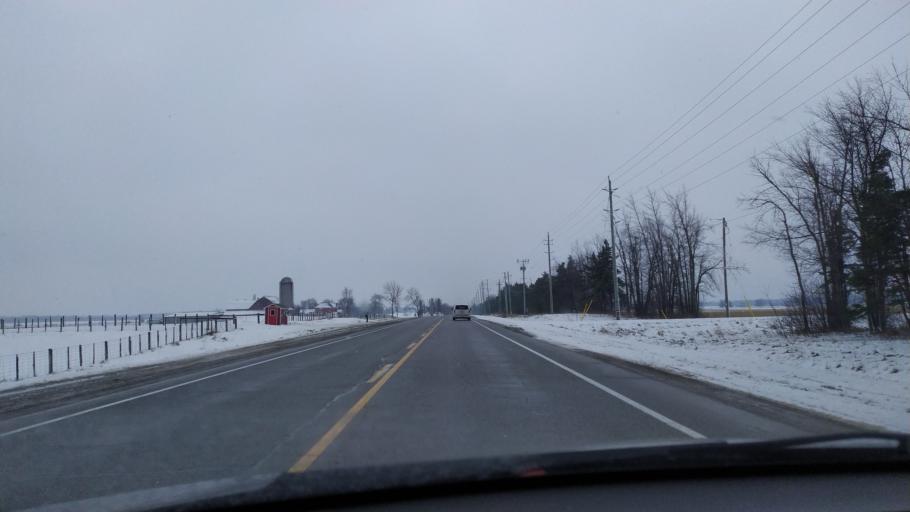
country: CA
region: Ontario
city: Waterloo
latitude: 43.6195
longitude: -80.6841
